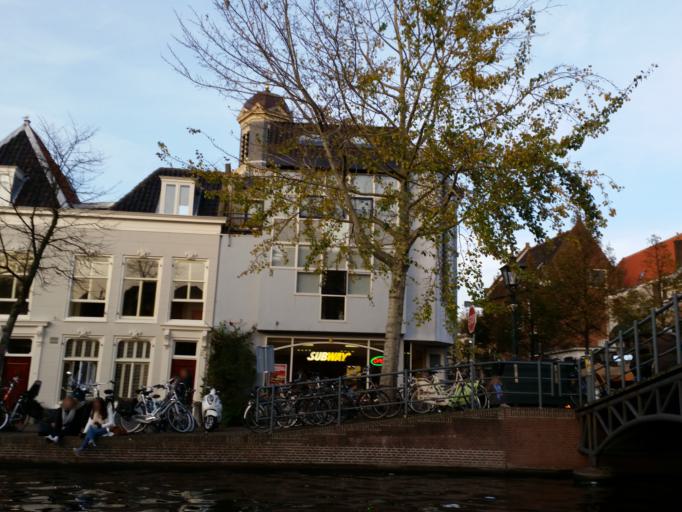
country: NL
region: South Holland
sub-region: Gemeente Leiden
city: Leiden
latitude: 52.1597
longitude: 4.4907
